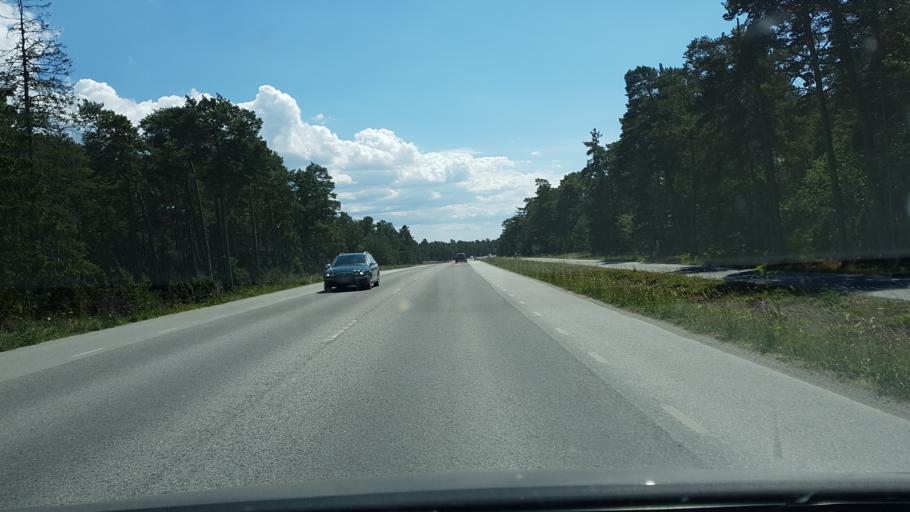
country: SE
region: Gotland
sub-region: Gotland
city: Vibble
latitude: 57.5543
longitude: 18.2029
